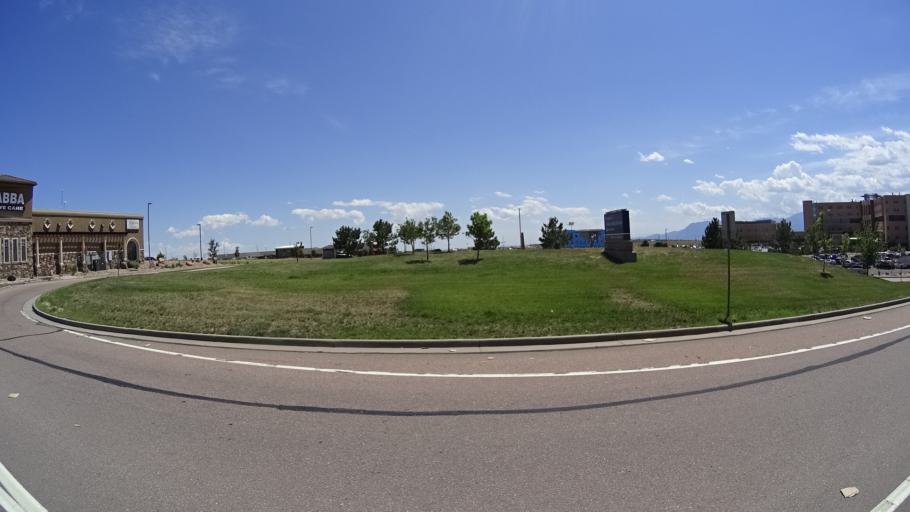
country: US
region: Colorado
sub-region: El Paso County
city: Black Forest
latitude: 38.9404
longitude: -104.7142
